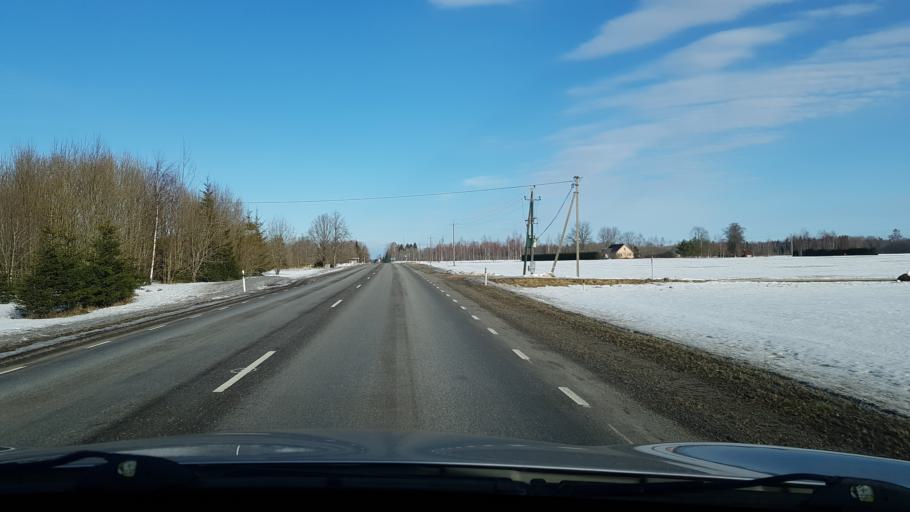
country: EE
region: Viljandimaa
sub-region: Viljandi linn
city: Viljandi
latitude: 58.4390
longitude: 25.5953
